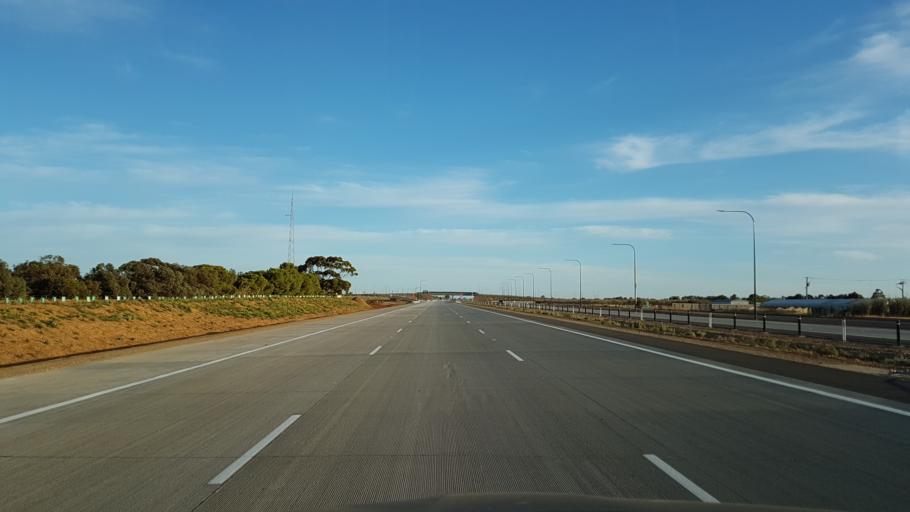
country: AU
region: South Australia
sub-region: Salisbury
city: Salisbury
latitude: -34.7408
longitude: 138.5792
